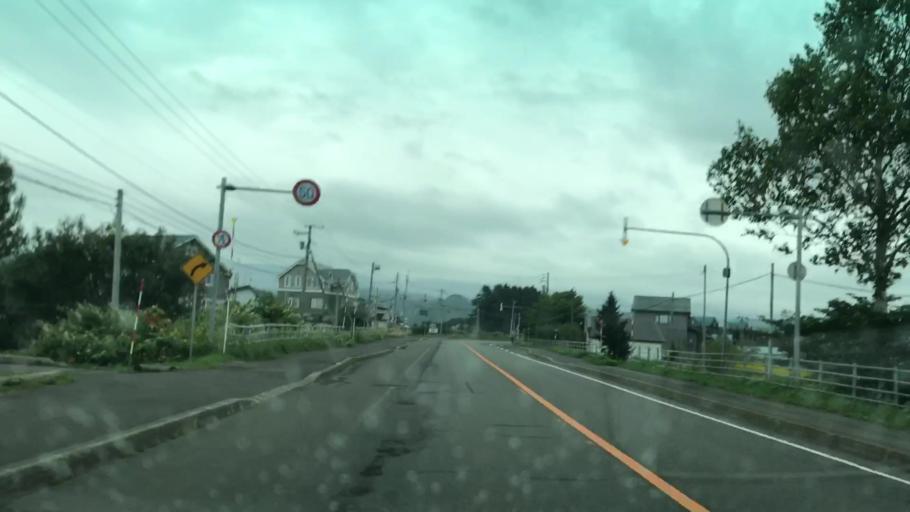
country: JP
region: Hokkaido
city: Niseko Town
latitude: 42.8120
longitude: 140.5431
